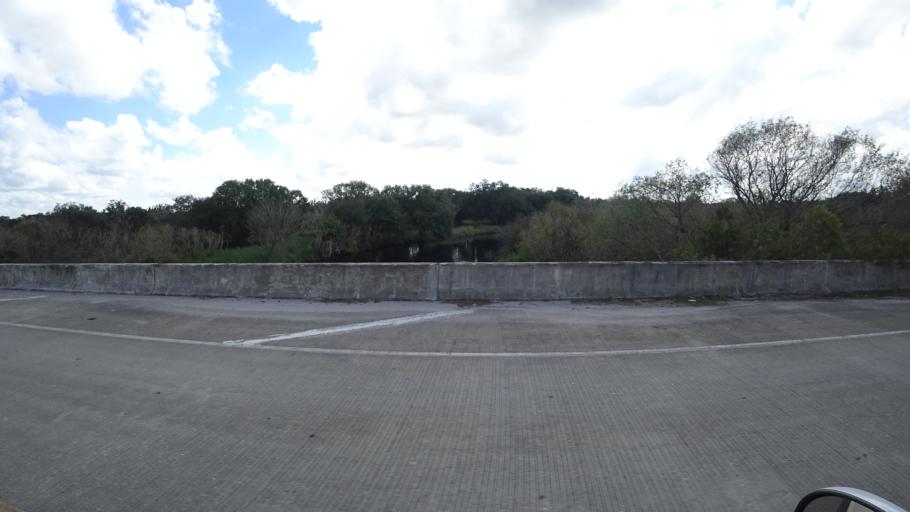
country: US
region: Florida
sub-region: Sarasota County
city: Lake Sarasota
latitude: 27.3659
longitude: -82.1491
